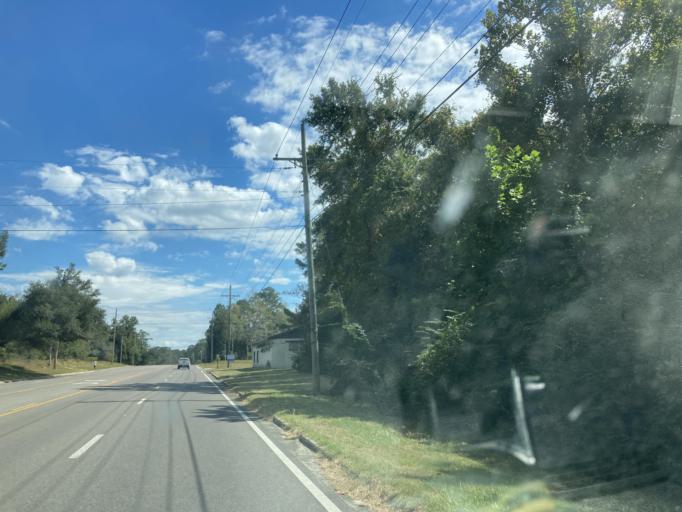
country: US
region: Mississippi
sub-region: Jackson County
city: Gulf Hills
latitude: 30.4431
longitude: -88.8479
